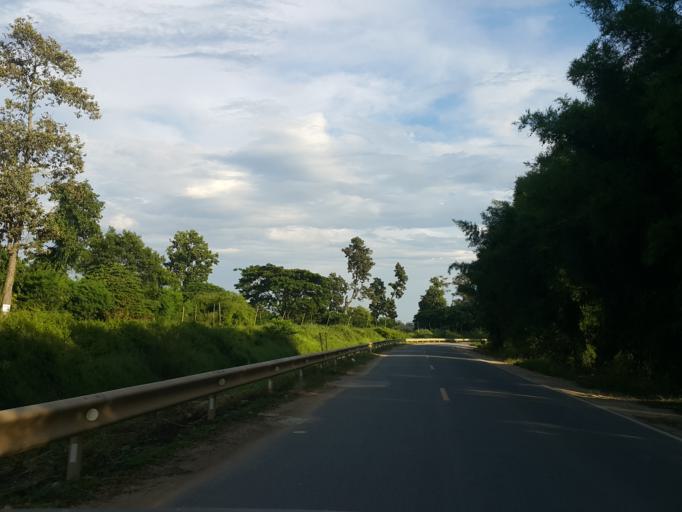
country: TH
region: Chiang Mai
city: San Sai
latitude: 18.9264
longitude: 98.9997
